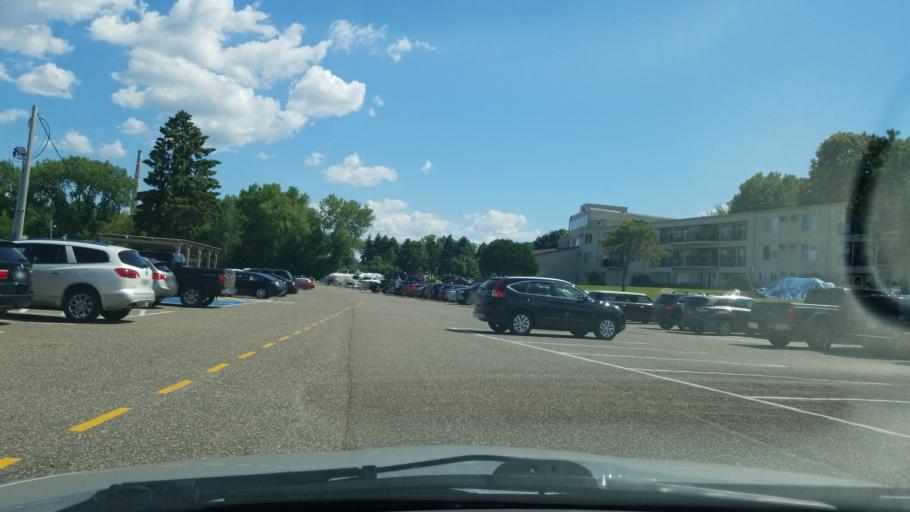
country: US
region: Minnesota
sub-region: Washington County
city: Oak Park Heights
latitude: 45.0409
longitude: -92.7920
